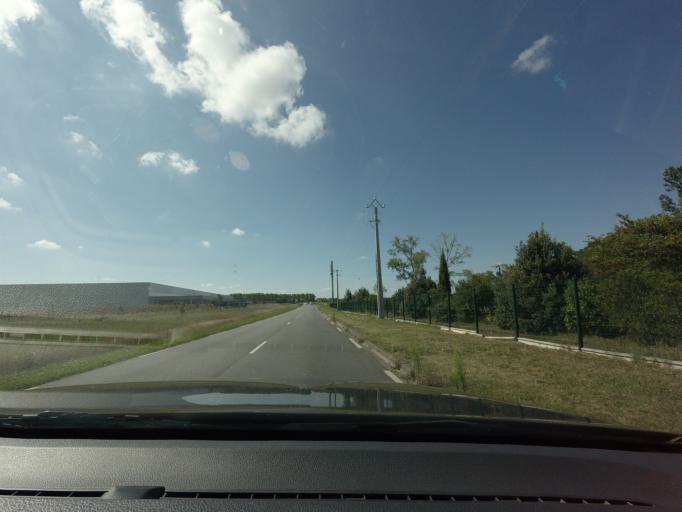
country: FR
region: Midi-Pyrenees
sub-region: Departement de la Haute-Garonne
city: Cornebarrieu
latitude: 43.6338
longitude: 1.3321
